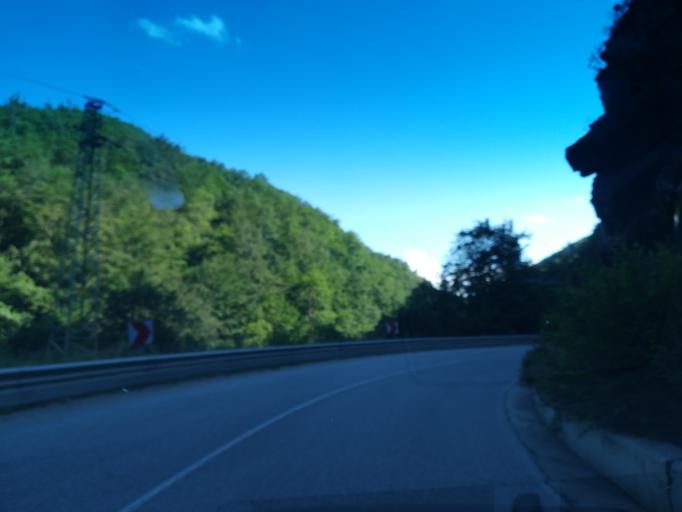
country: BG
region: Smolyan
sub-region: Obshtina Chepelare
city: Chepelare
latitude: 41.7852
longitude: 24.7085
